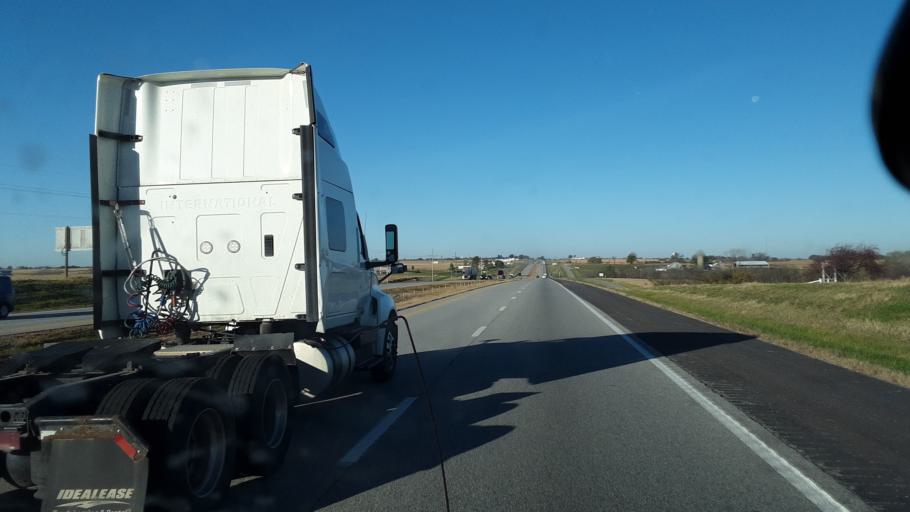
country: US
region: Missouri
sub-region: Lafayette County
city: Concordia
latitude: 38.9880
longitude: -93.5195
